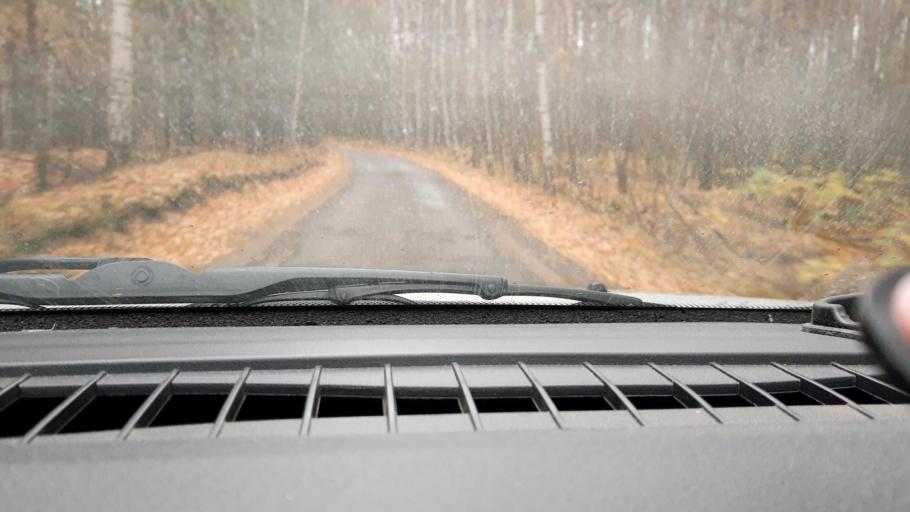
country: RU
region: Nizjnij Novgorod
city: Sitniki
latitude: 56.4219
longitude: 44.0479
